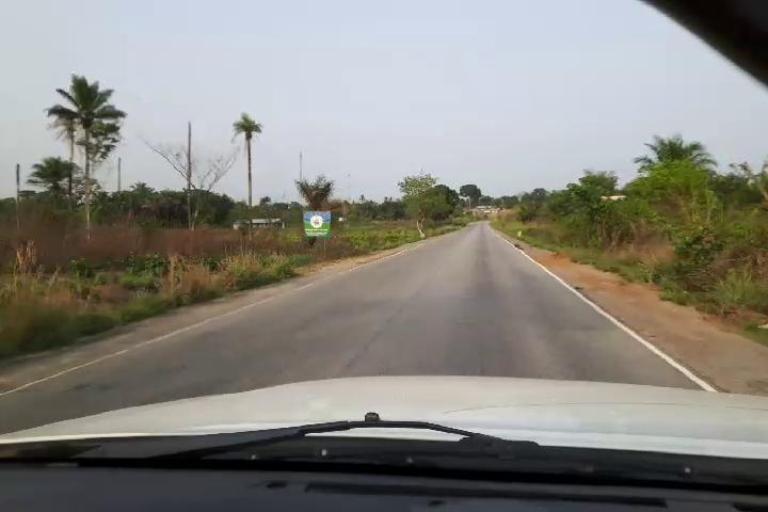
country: SL
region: Southern Province
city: Baoma
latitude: 7.9291
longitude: -11.5784
